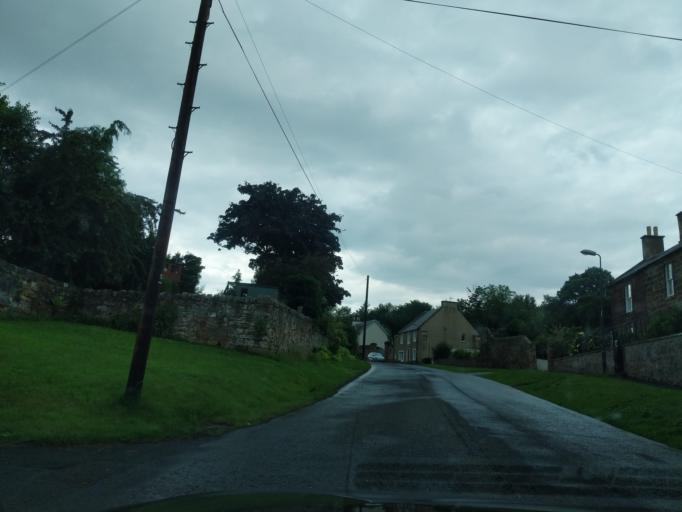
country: GB
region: Scotland
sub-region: Midlothian
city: Dalkeith
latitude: 55.8977
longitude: -3.0758
